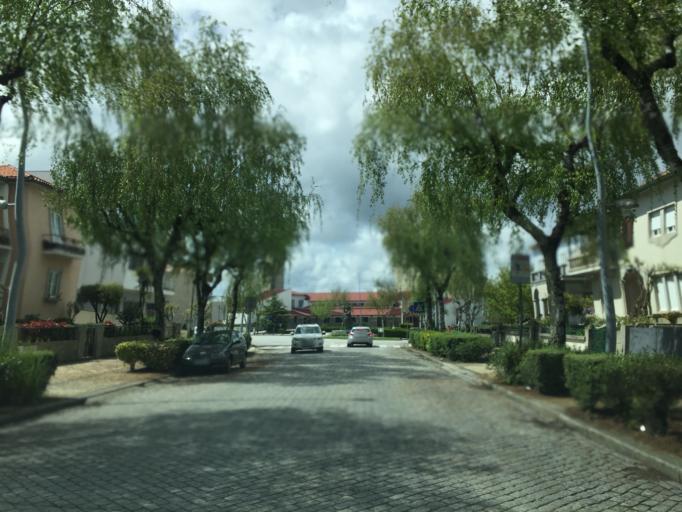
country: PT
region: Viseu
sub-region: Viseu
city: Viseu
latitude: 40.6564
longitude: -7.9197
